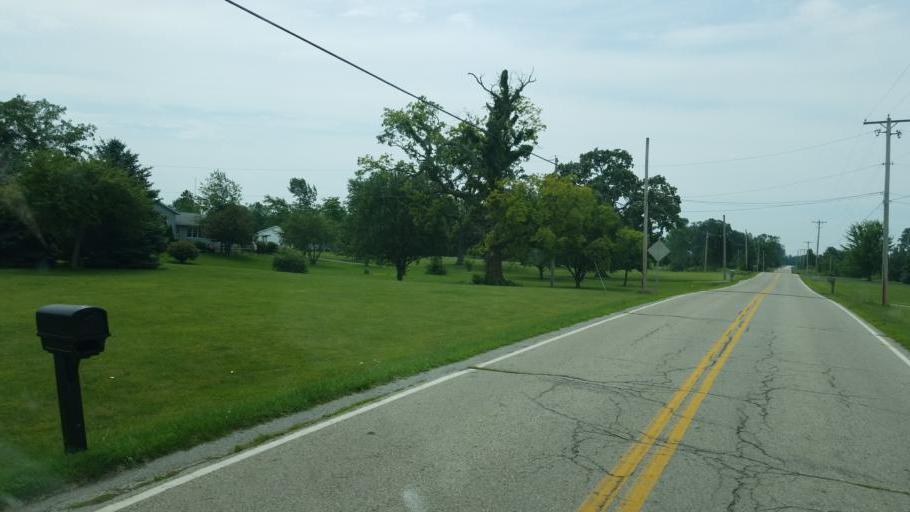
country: US
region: Ohio
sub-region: Madison County
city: Choctaw Lake
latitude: 40.0217
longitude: -83.3911
